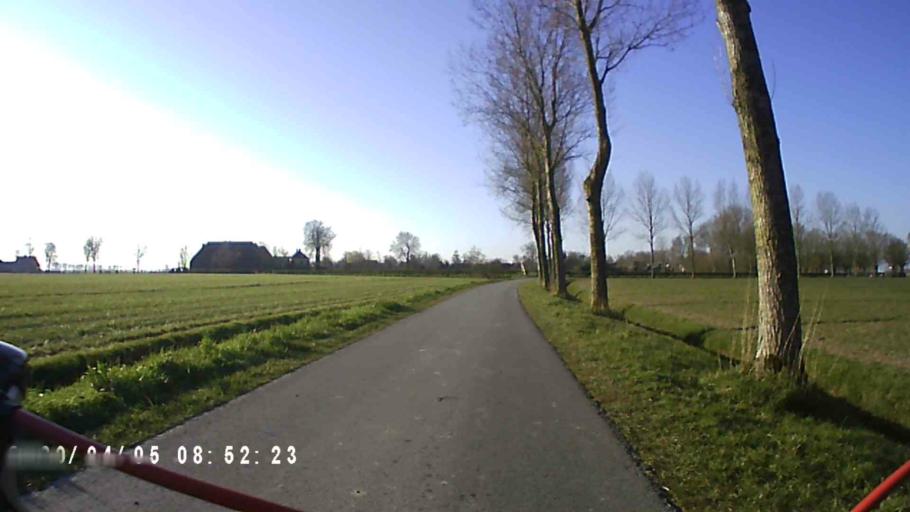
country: NL
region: Groningen
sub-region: Gemeente Zuidhorn
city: Aduard
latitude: 53.3106
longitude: 6.4655
